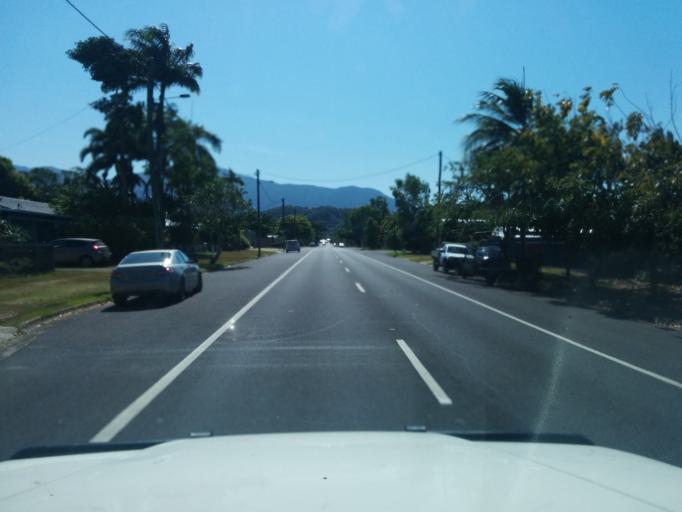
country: AU
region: Queensland
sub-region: Cairns
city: Cairns
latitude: -16.9029
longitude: 145.7399
